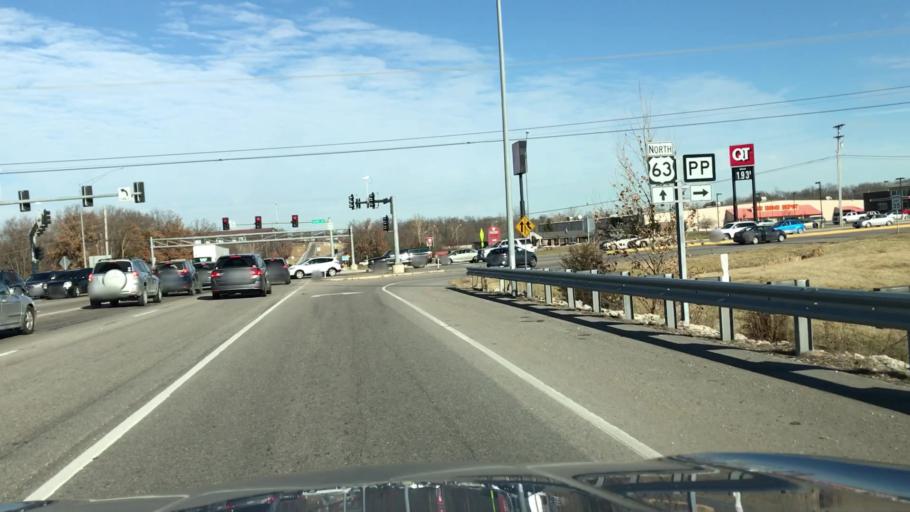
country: US
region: Missouri
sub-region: Boone County
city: Columbia
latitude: 38.9631
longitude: -92.2918
